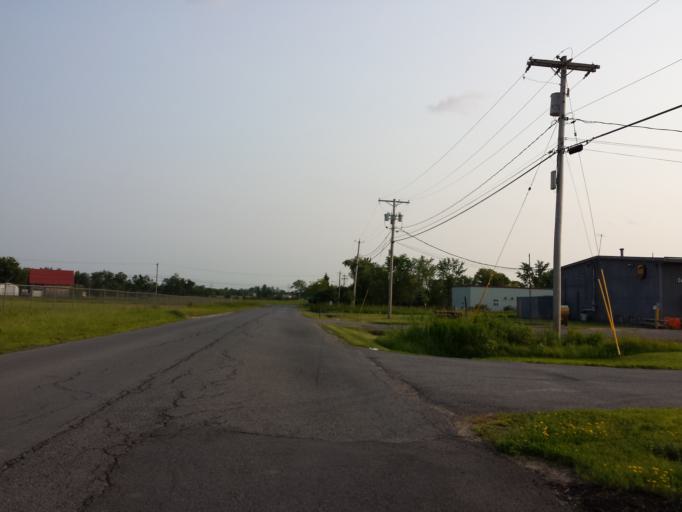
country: US
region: New York
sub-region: St. Lawrence County
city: Potsdam
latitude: 44.6717
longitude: -74.9569
